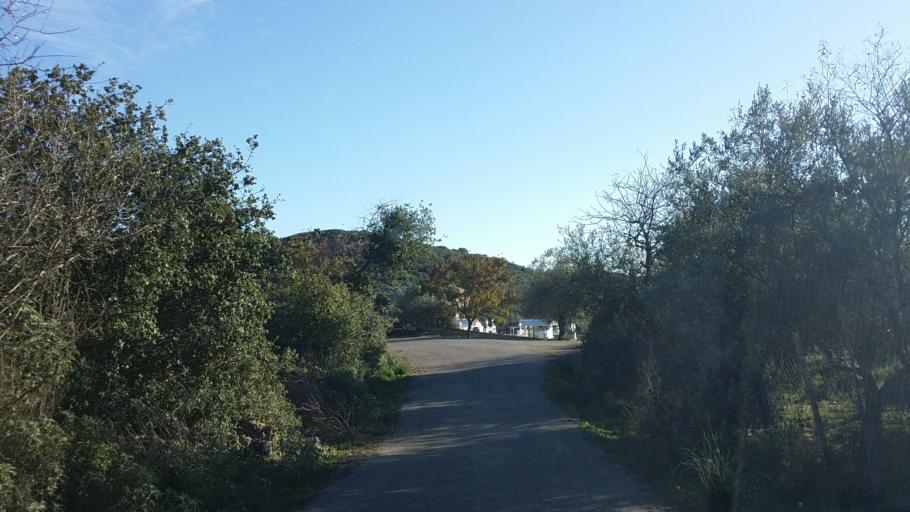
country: GR
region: West Greece
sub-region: Nomos Aitolias kai Akarnanias
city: Fitiai
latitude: 38.7055
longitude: 21.1775
